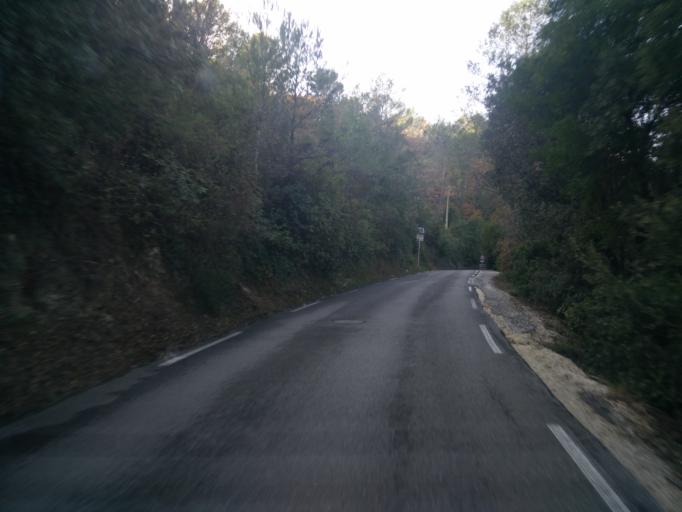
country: FR
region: Provence-Alpes-Cote d'Azur
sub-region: Departement du Var
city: Sollies-Toucas
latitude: 43.2034
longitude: 6.0137
